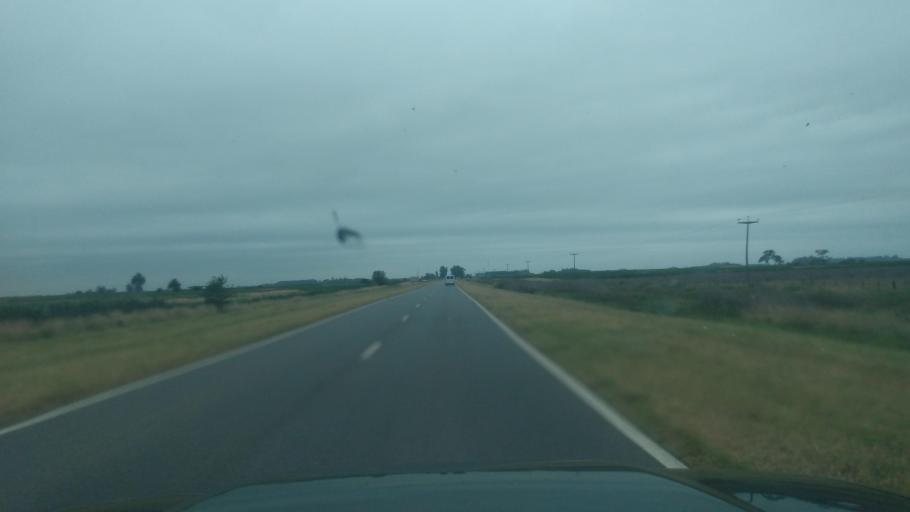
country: AR
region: Buenos Aires
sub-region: Partido de Nueve de Julio
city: Nueve de Julio
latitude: -35.3743
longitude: -60.7189
